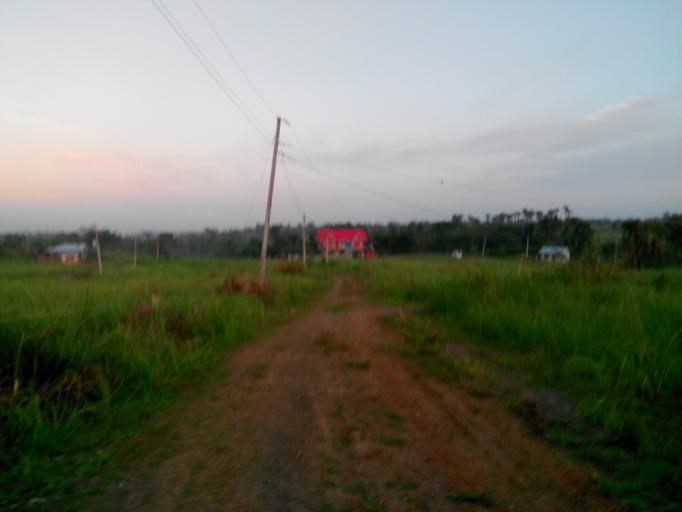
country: PH
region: Western Visayas
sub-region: Province of Iloilo
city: Passi
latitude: 11.1219
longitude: 122.6489
